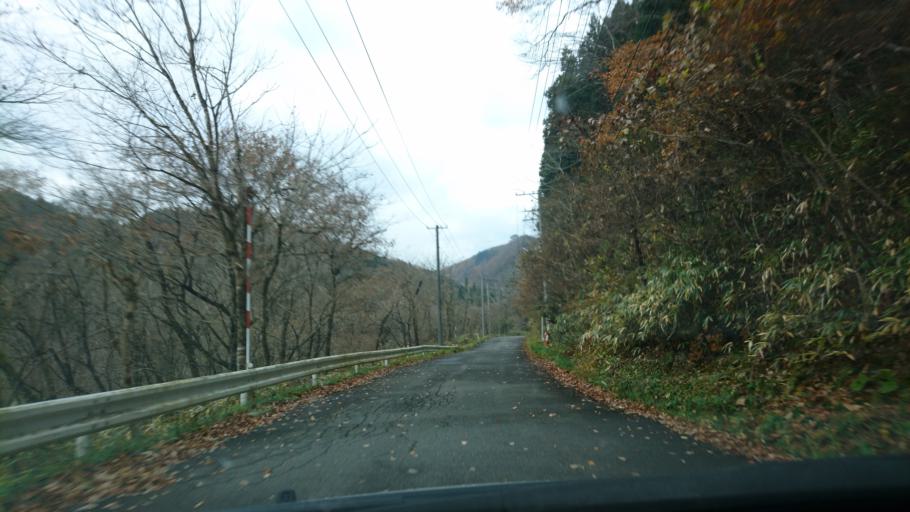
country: JP
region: Iwate
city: Ichinoseki
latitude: 38.9070
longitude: 140.9001
